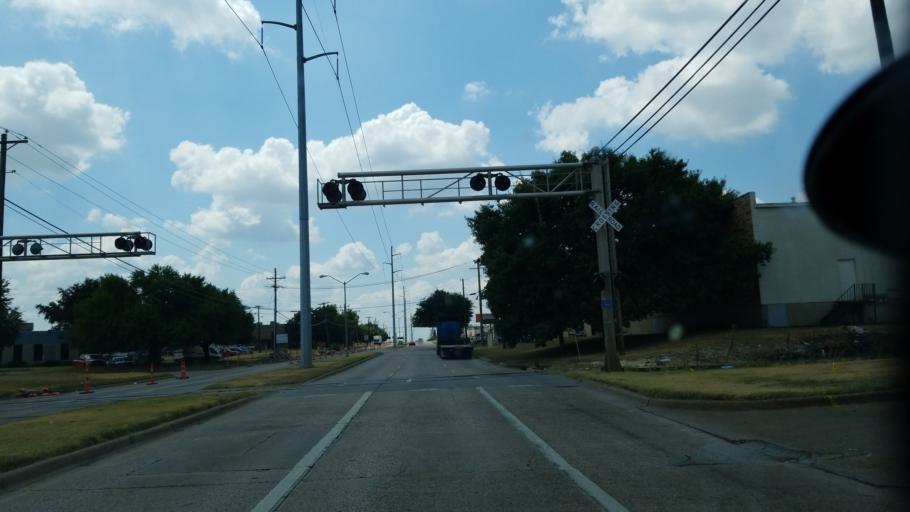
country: US
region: Texas
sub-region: Dallas County
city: Duncanville
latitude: 32.6866
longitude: -96.8915
